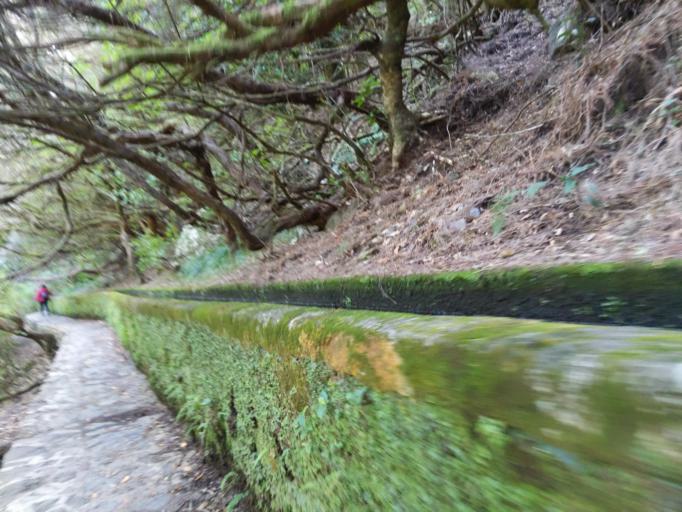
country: PT
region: Madeira
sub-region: Calheta
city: Arco da Calheta
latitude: 32.7663
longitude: -17.1287
